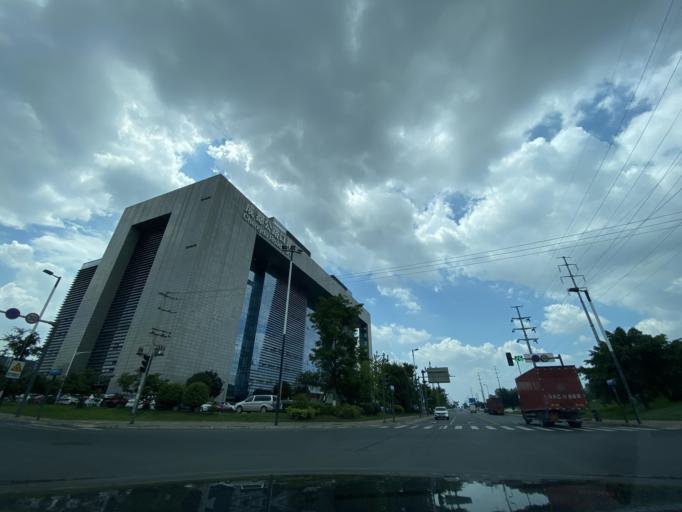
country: CN
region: Sichuan
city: Longquan
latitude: 30.5335
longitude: 104.1969
